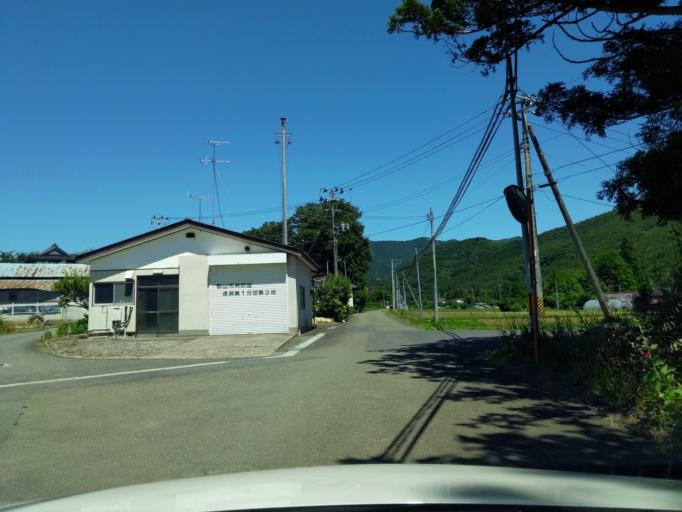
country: JP
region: Fukushima
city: Koriyama
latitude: 37.4101
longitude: 140.2371
